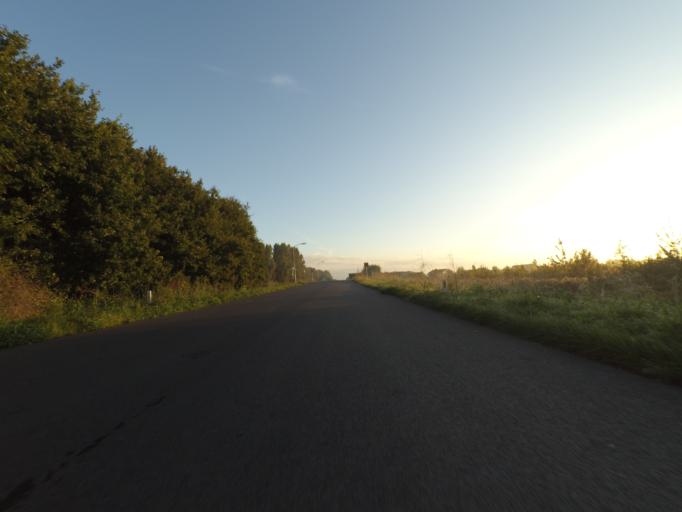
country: NL
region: Flevoland
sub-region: Gemeente Zeewolde
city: Zeewolde
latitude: 52.3451
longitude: 5.4778
